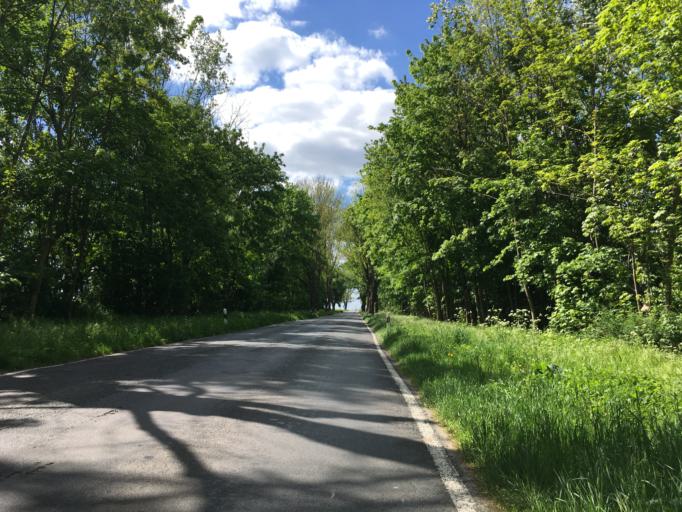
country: DE
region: Brandenburg
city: Rudnitz
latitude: 52.6661
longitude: 13.6607
